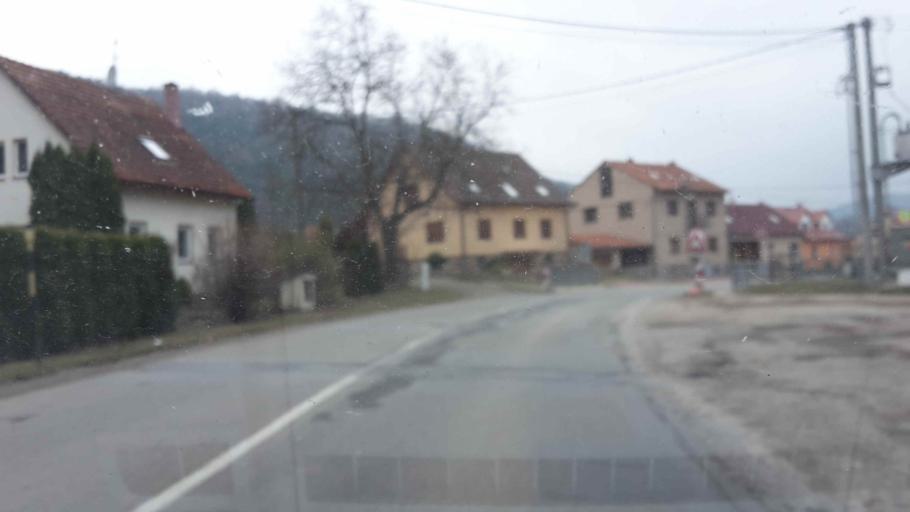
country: CZ
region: South Moravian
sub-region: Okres Brno-Venkov
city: Dolni Loucky
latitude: 49.3786
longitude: 16.3797
